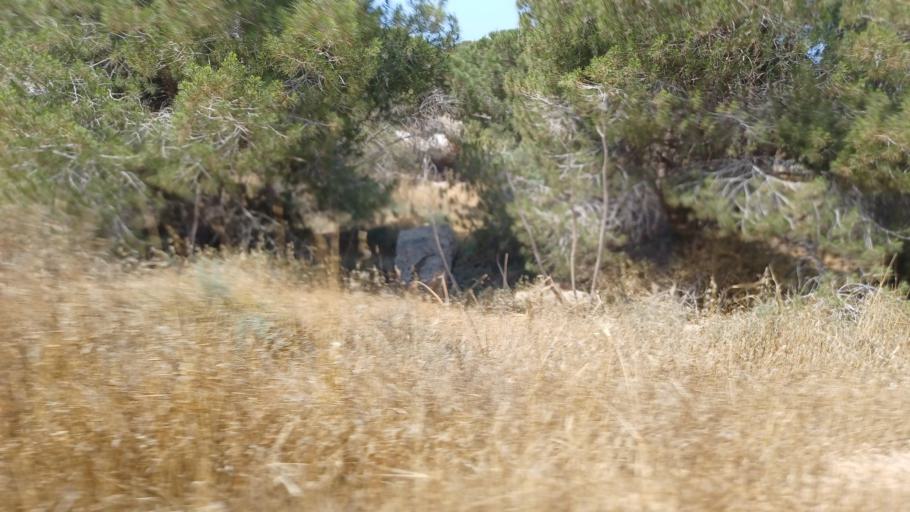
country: CY
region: Ammochostos
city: Paralimni
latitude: 35.0031
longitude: 33.9687
